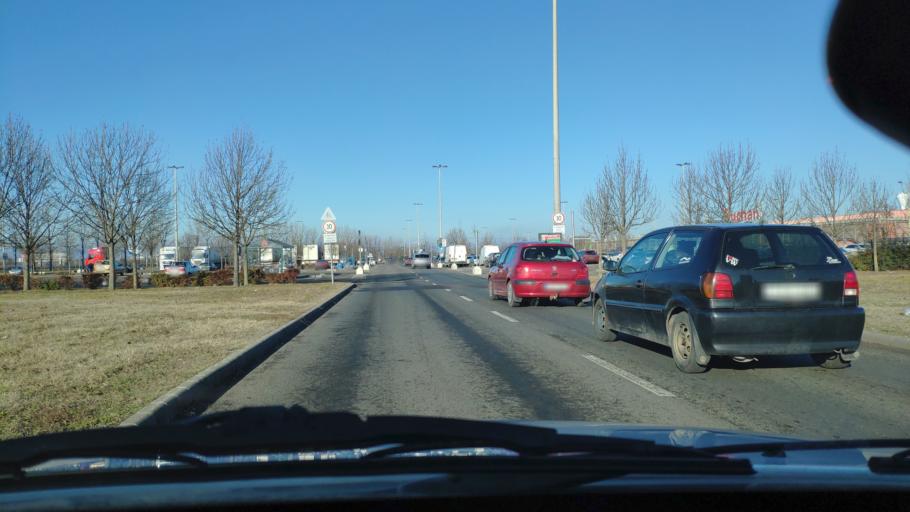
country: HU
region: Budapest
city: Budapest XVIII. keruelet
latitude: 47.4166
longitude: 19.1581
